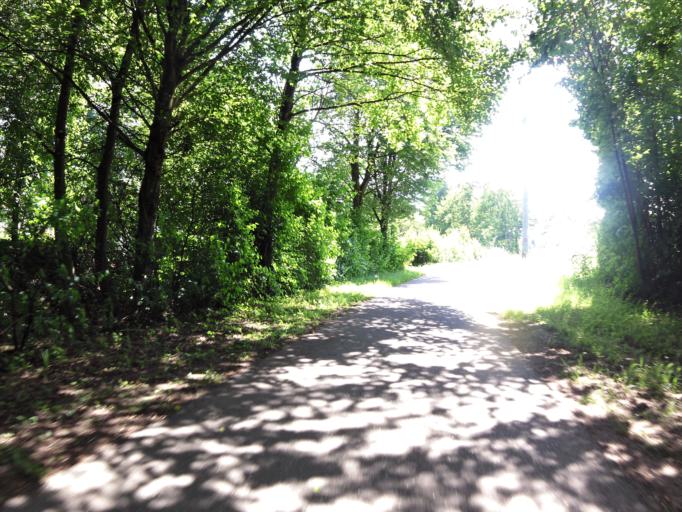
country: DE
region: Baden-Wuerttemberg
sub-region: Freiburg Region
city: Hohberg
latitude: 48.3336
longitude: 7.9150
